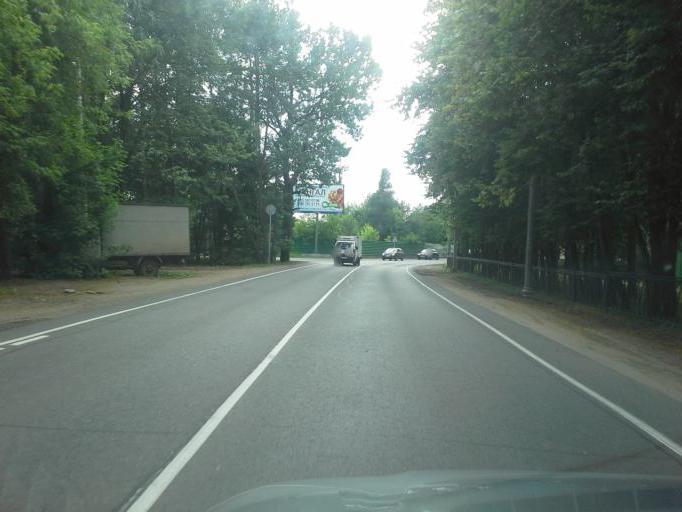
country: RU
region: Moskovskaya
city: Barvikha
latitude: 55.7227
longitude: 37.2745
